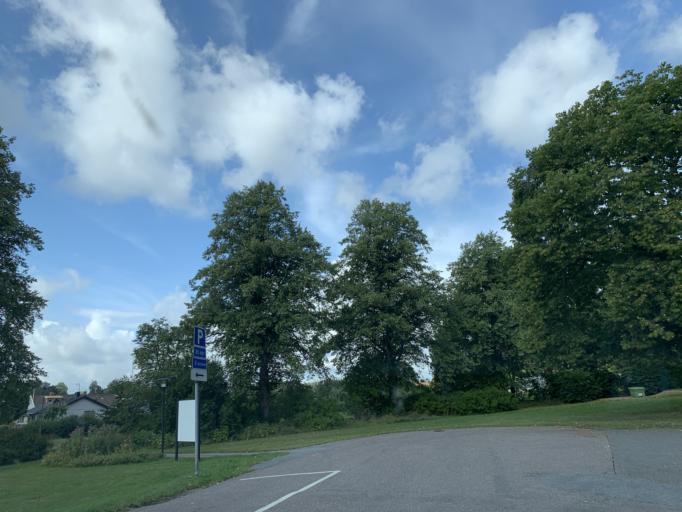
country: SE
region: Vaestra Goetaland
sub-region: Goteborg
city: Eriksbo
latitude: 57.7420
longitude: 12.0602
